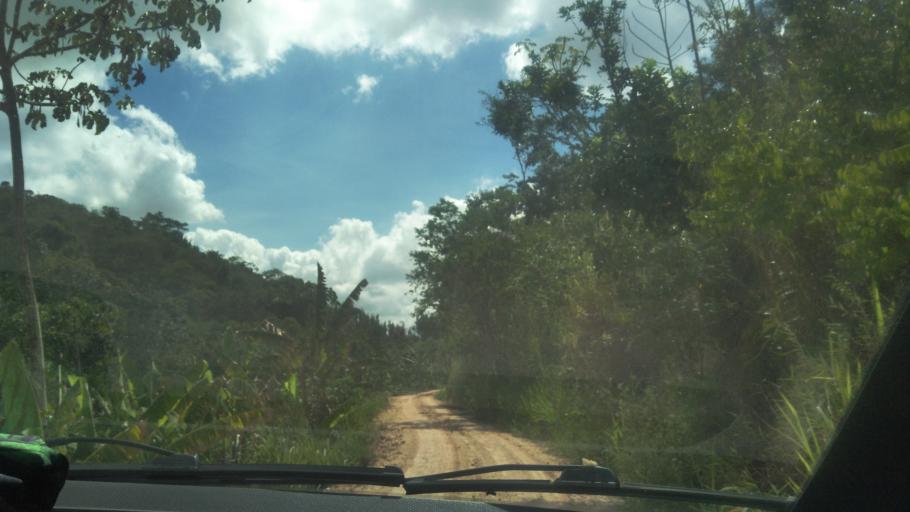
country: BR
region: Pernambuco
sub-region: Vitoria De Santo Antao
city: Vitoria de Santo Antao
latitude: -8.1463
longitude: -35.2548
